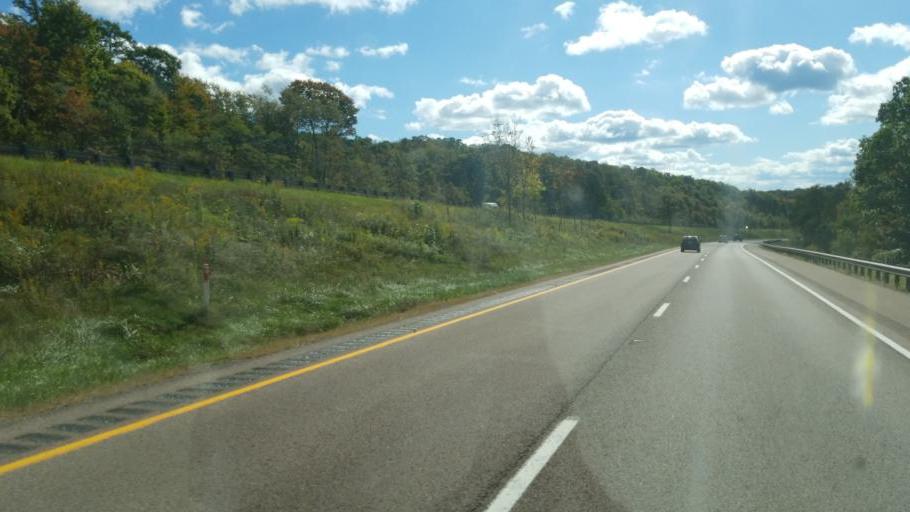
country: US
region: Maryland
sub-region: Garrett County
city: Oakland
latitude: 39.6916
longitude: -79.3443
